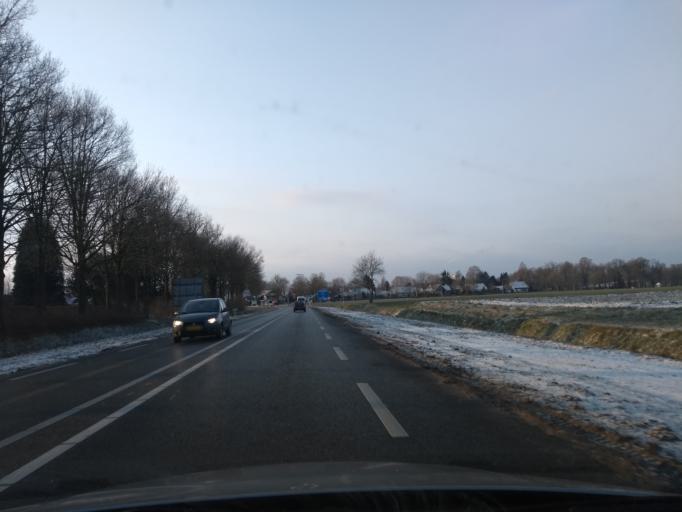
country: NL
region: Overijssel
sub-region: Gemeente Hof van Twente
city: Delden
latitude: 52.2625
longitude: 6.7019
